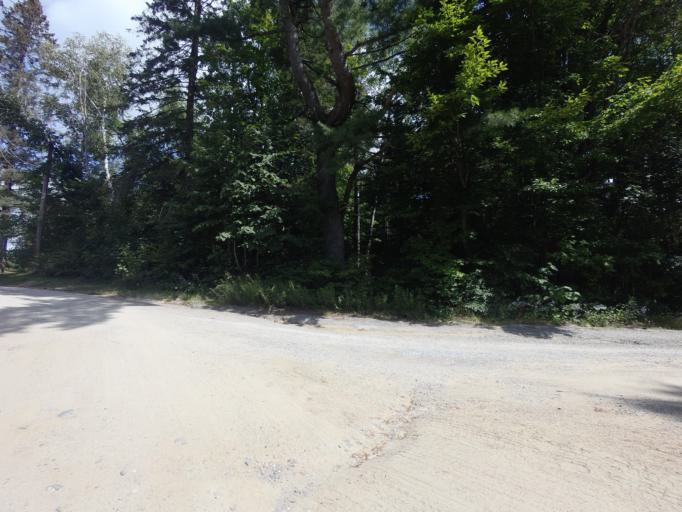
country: CA
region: Ontario
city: Omemee
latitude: 44.8279
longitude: -78.5619
